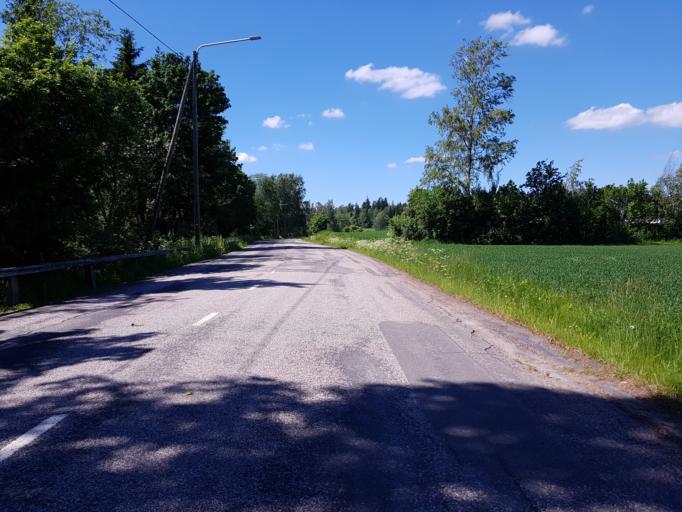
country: FI
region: Uusimaa
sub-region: Helsinki
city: Teekkarikylae
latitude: 60.2932
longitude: 24.8812
